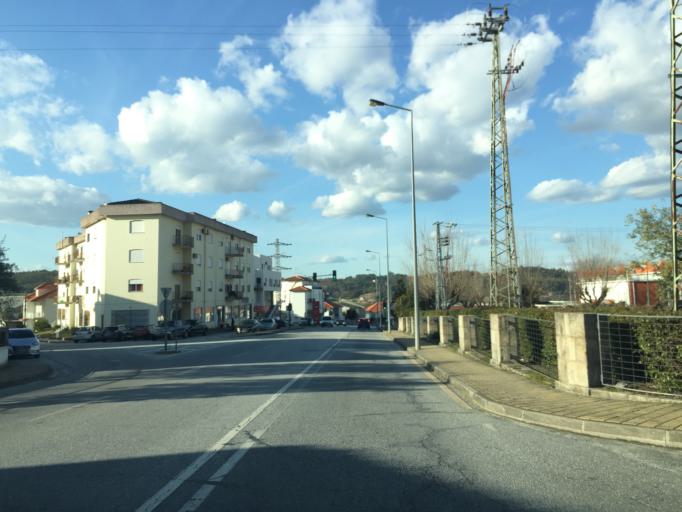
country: PT
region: Guarda
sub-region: Seia
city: Seia
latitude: 40.4234
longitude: -7.7140
